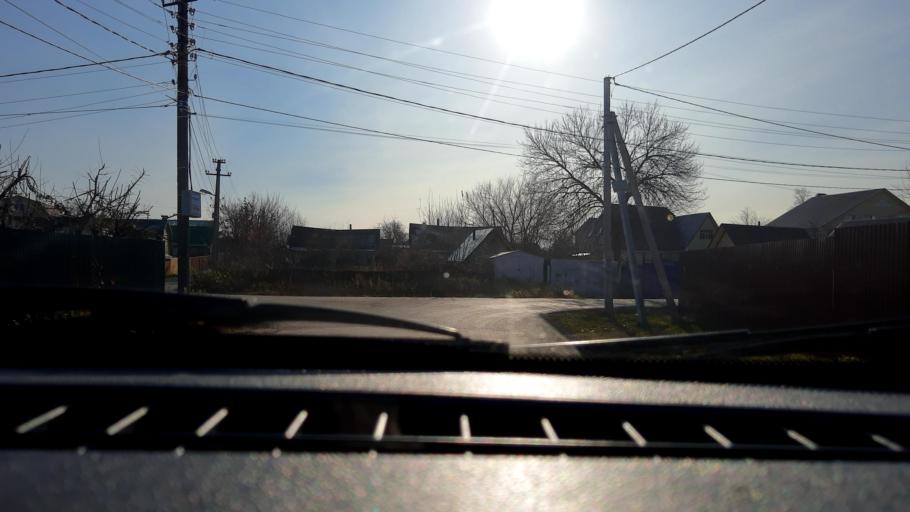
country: RU
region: Bashkortostan
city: Mikhaylovka
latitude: 54.7593
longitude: 55.9066
